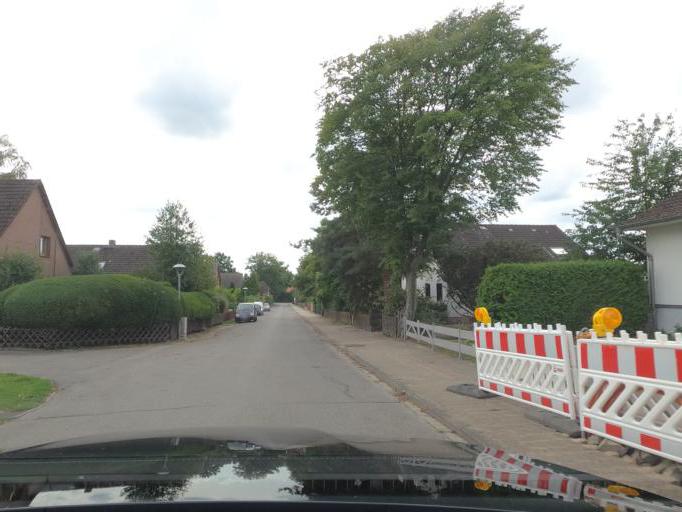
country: DE
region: Lower Saxony
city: Isernhagen Farster Bauerschaft
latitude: 52.5152
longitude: 9.9234
